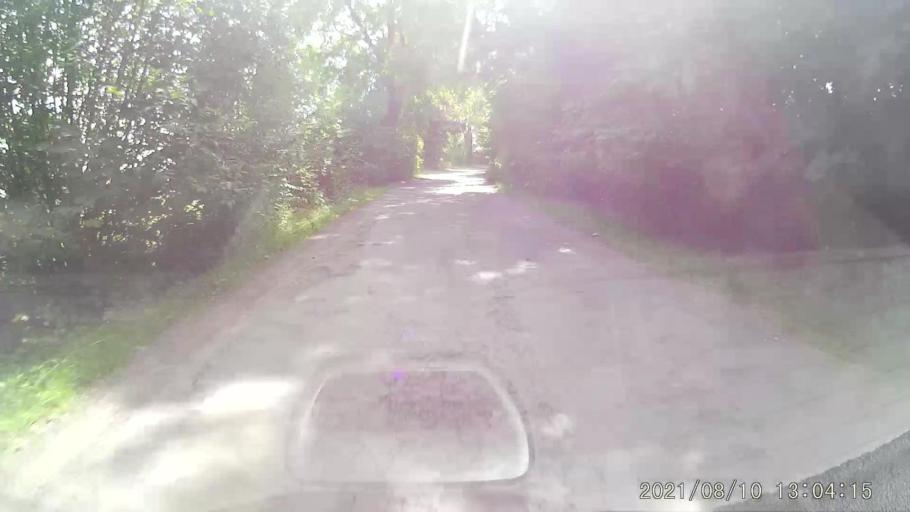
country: PL
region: Lower Silesian Voivodeship
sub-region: Powiat klodzki
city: Bozkow
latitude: 50.4758
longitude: 16.5647
